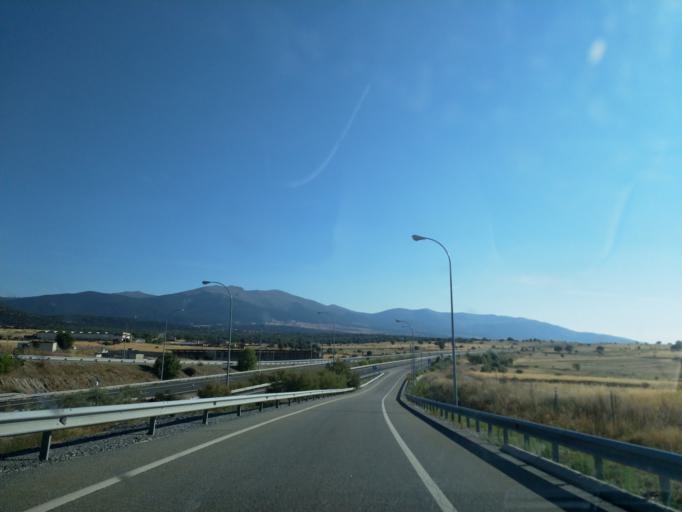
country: ES
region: Castille and Leon
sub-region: Provincia de Segovia
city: Segovia
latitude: 40.9037
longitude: -4.1043
